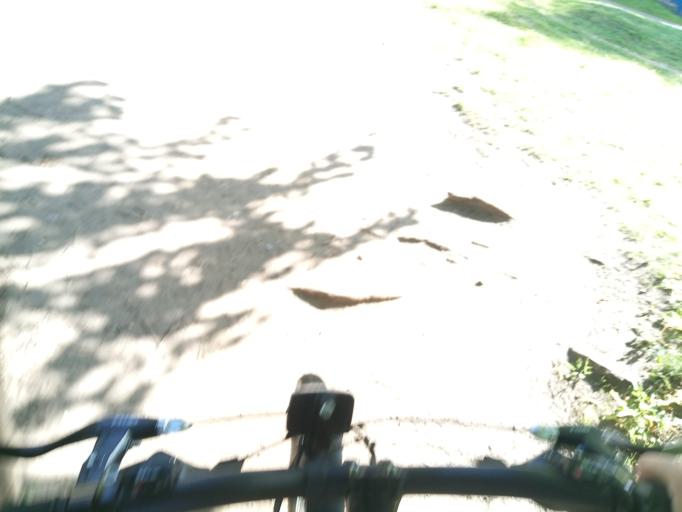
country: RU
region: Jaroslavl
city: Yaroslavl
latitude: 57.6535
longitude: 39.9561
